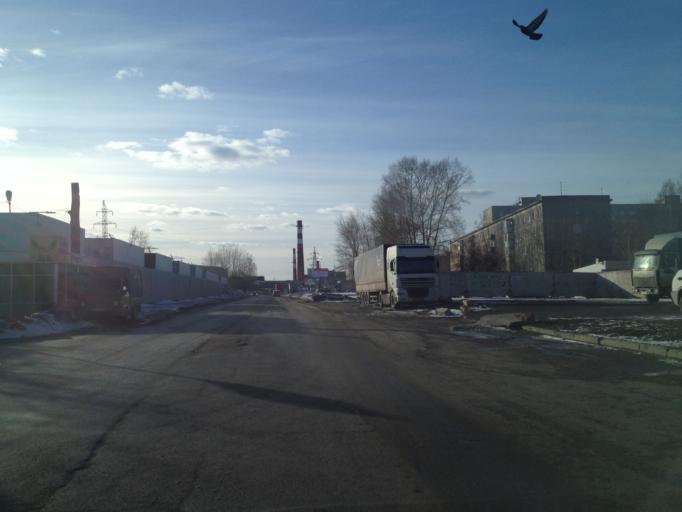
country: RU
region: Sverdlovsk
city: Yekaterinburg
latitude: 56.8625
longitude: 60.5349
